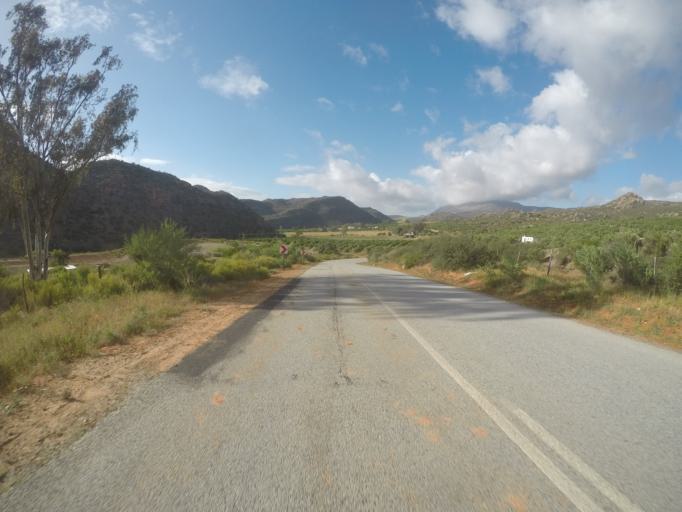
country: ZA
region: Western Cape
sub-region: West Coast District Municipality
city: Clanwilliam
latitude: -32.4321
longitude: 18.9392
